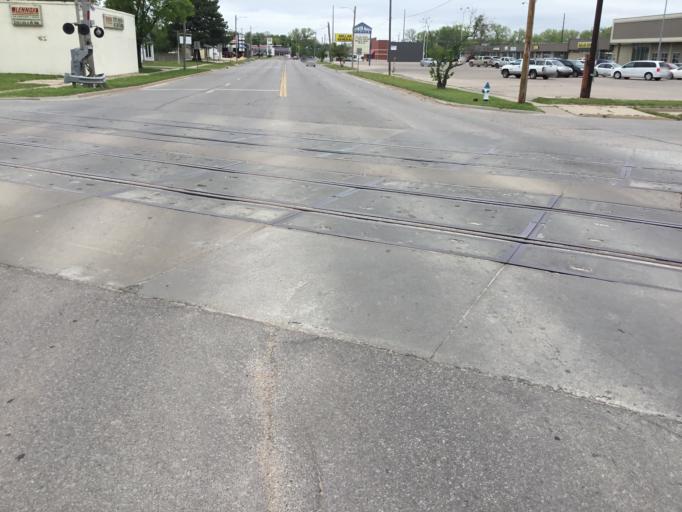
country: US
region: Kansas
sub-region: Butler County
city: El Dorado
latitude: 37.8220
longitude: -96.8499
